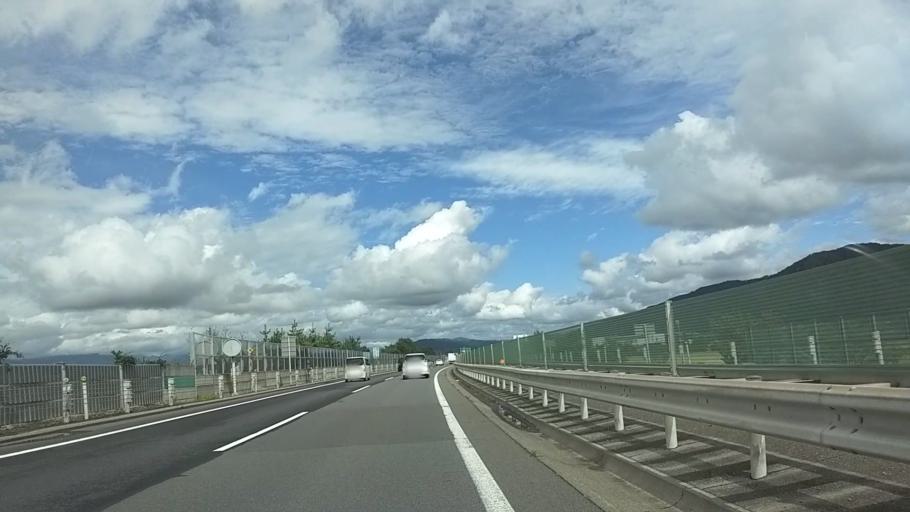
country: JP
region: Nagano
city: Toyoshina
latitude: 36.2880
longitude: 137.9283
